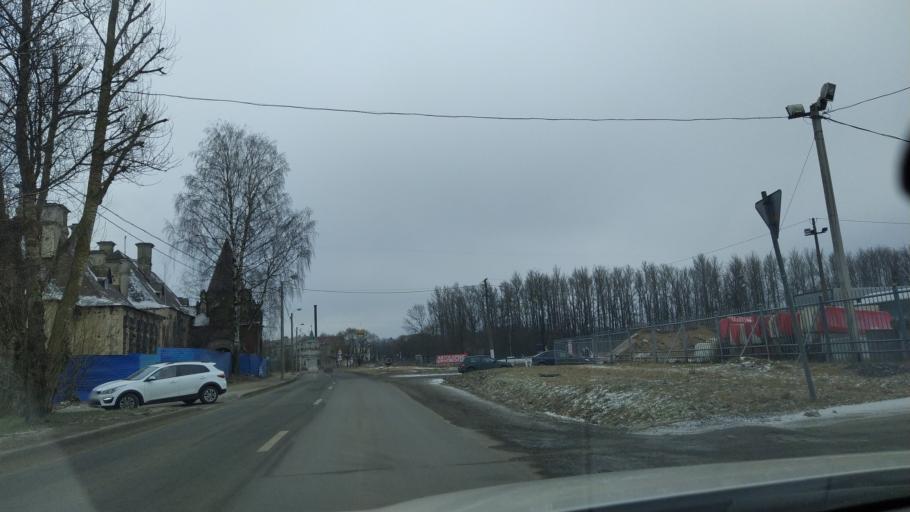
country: RU
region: St.-Petersburg
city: Pushkin
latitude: 59.7316
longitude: 30.3833
